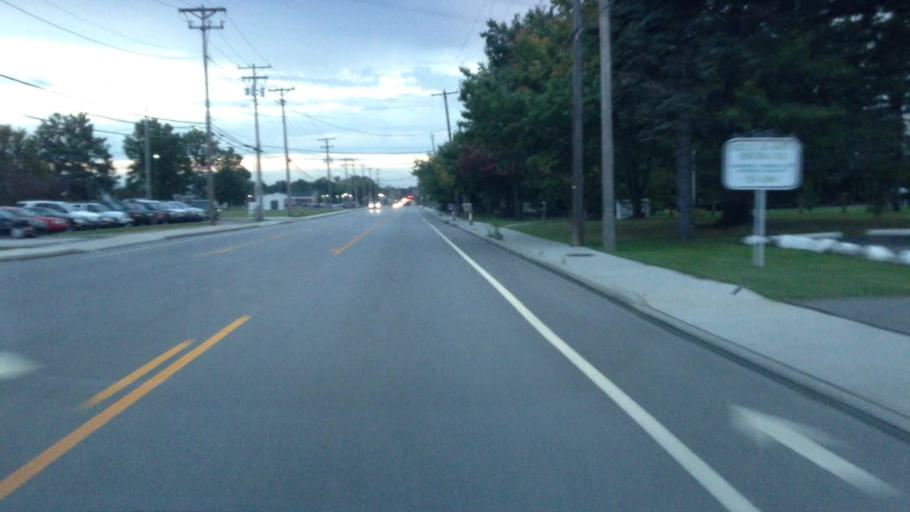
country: US
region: Ohio
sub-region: Summit County
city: Cuyahoga Falls
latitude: 41.1769
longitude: -81.5086
